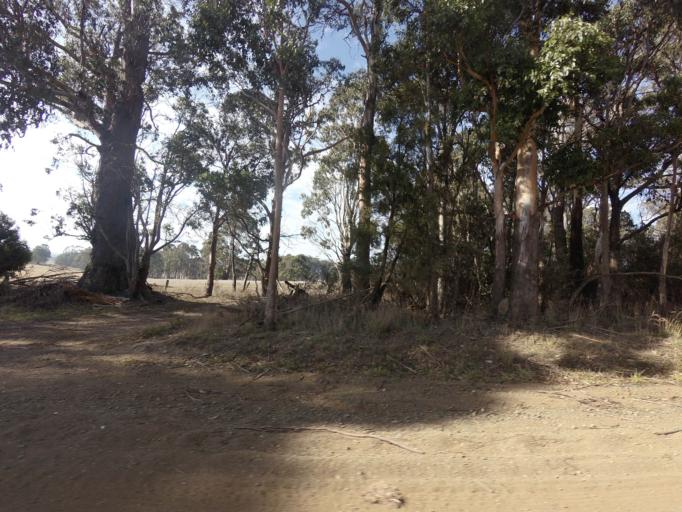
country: AU
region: Tasmania
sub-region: Sorell
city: Sorell
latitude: -42.4752
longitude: 147.4749
